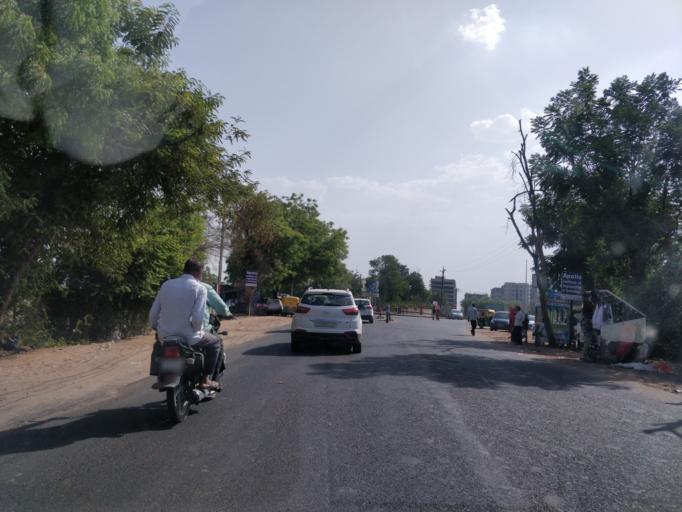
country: IN
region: Gujarat
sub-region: Ahmadabad
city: Naroda
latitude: 23.0897
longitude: 72.6880
